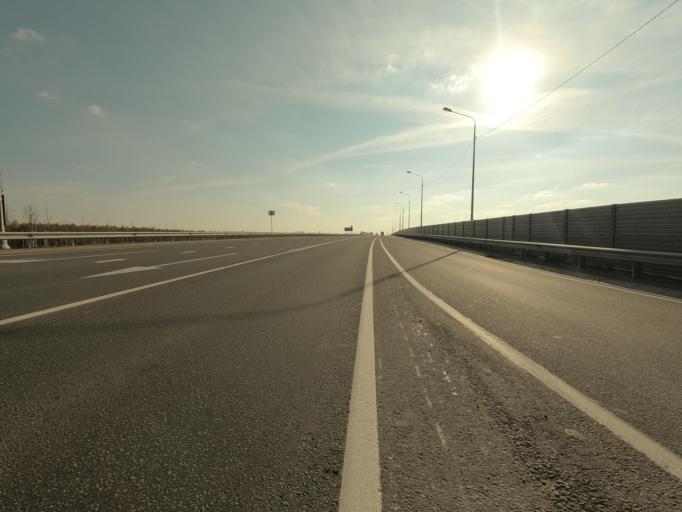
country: RU
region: Leningrad
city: Mga
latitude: 59.7571
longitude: 31.0932
